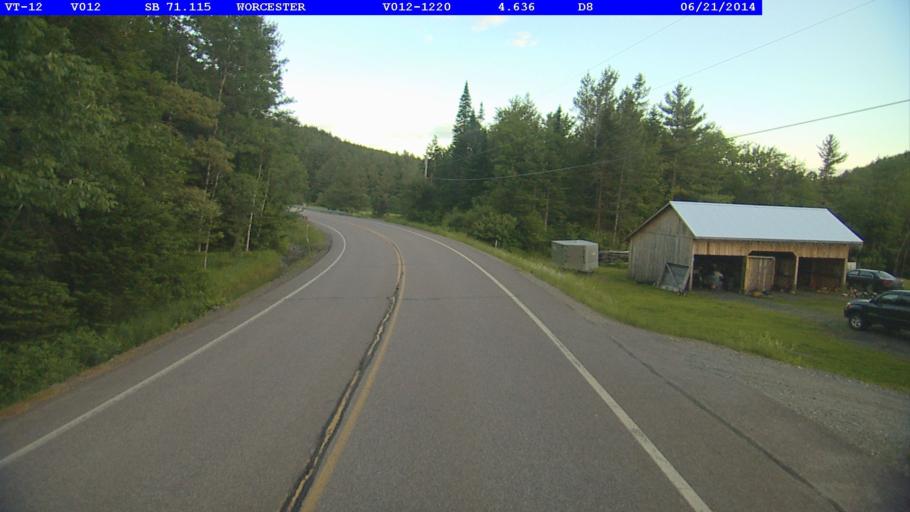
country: US
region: Vermont
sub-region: Washington County
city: Montpelier
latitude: 44.4124
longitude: -72.5492
